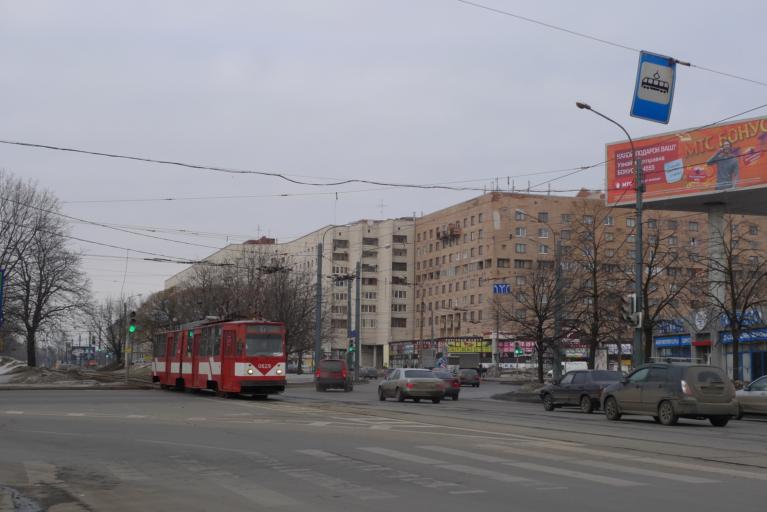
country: RU
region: St.-Petersburg
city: Kushelevka
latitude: 59.9971
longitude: 30.3640
